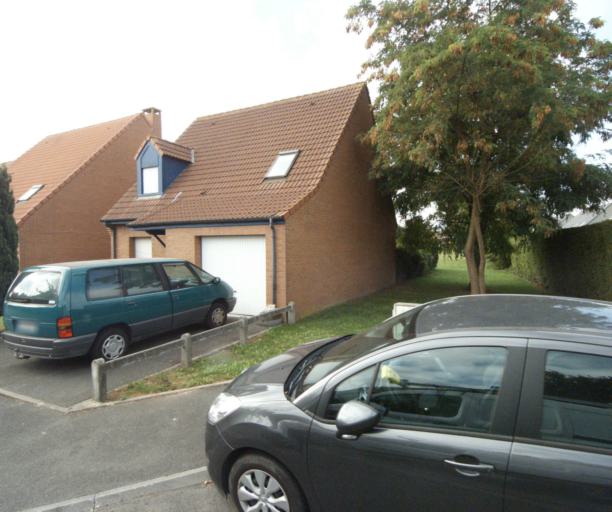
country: FR
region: Nord-Pas-de-Calais
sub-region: Departement du Nord
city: Villeneuve-d'Ascq
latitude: 50.6217
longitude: 3.1538
